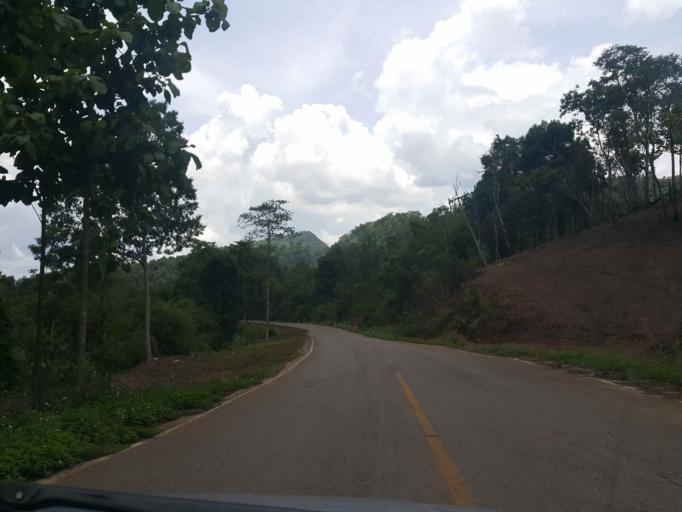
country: TH
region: Phayao
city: Chiang Muan
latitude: 18.9041
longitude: 100.1224
